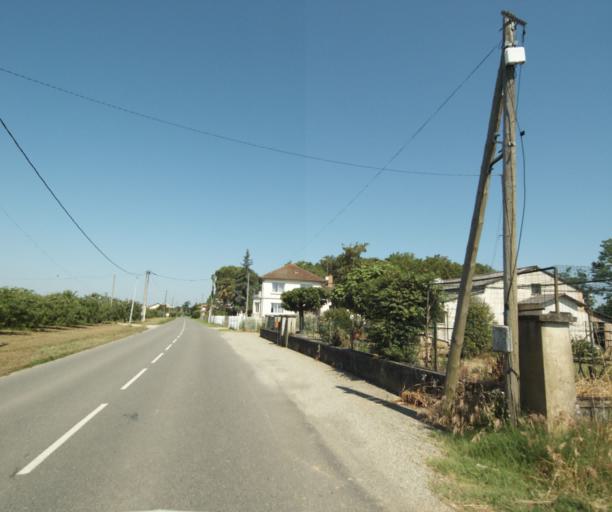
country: FR
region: Midi-Pyrenees
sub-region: Departement du Tarn-et-Garonne
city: Montbeton
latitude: 44.0313
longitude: 1.3060
